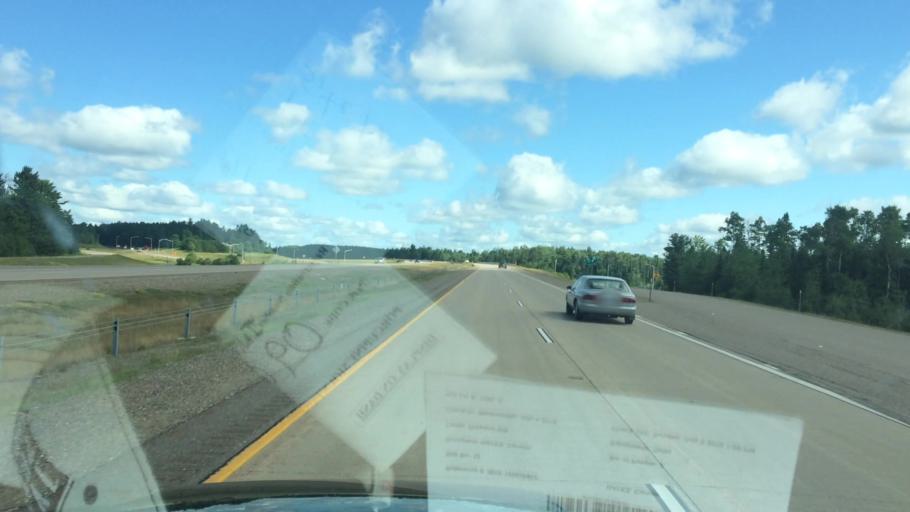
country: US
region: Wisconsin
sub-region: Lincoln County
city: Tomahawk
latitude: 45.4134
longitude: -89.6713
